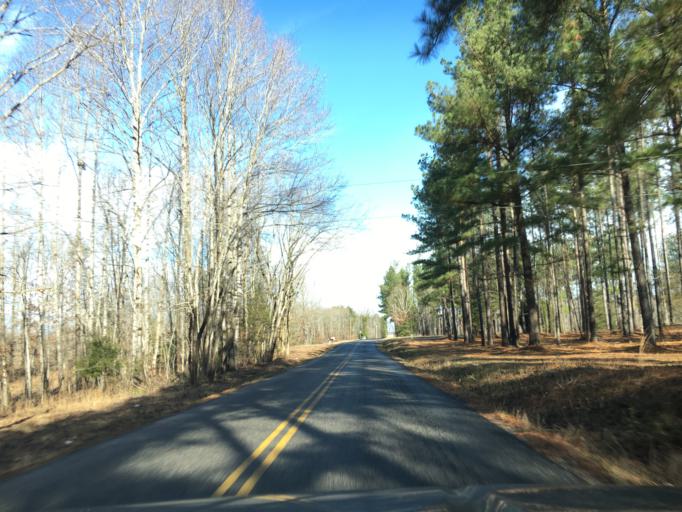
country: US
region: Virginia
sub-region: Amelia County
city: Amelia Court House
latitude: 37.4063
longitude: -78.0888
